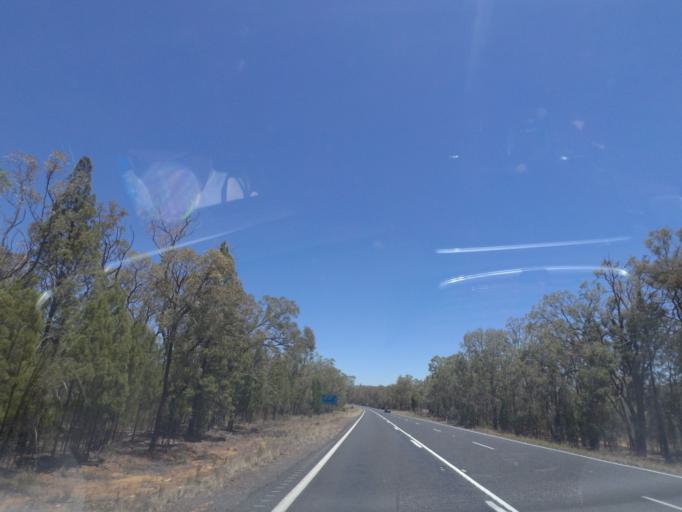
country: AU
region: New South Wales
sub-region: Warrumbungle Shire
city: Coonabarabran
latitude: -31.2374
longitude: 149.3153
